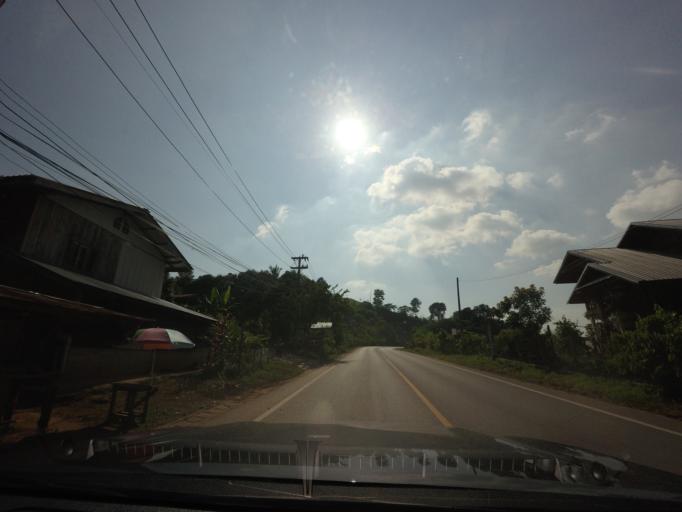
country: TH
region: Nan
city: Santi Suk
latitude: 18.9147
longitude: 100.8836
